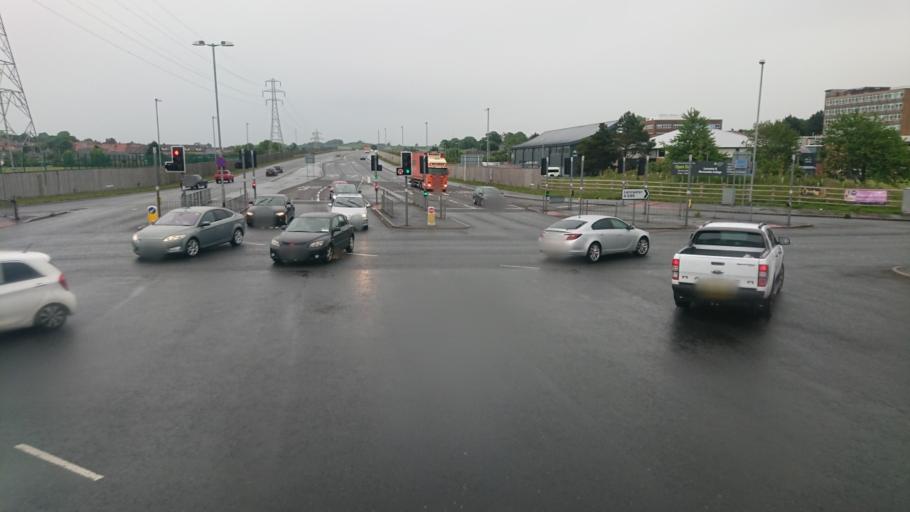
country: GB
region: England
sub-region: Lancashire
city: Morecambe
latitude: 54.0622
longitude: -2.8304
